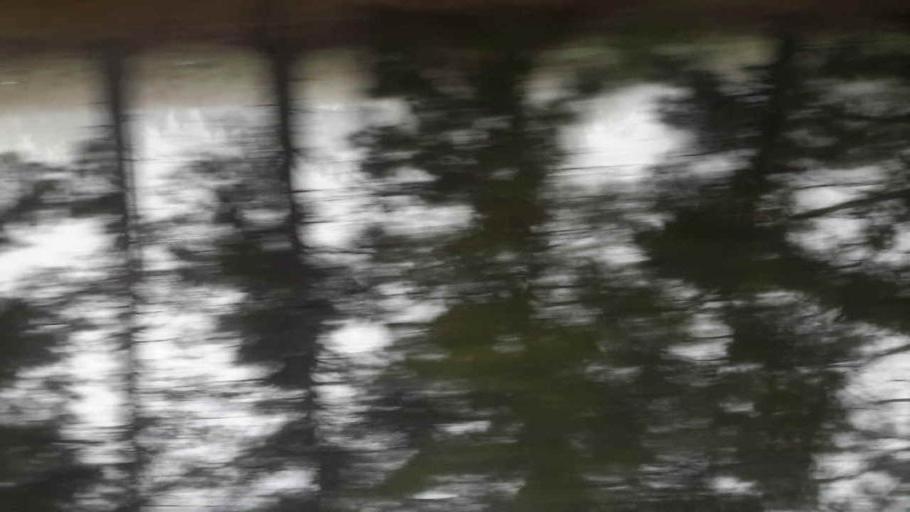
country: AU
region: New South Wales
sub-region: Wollondilly
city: Douglas Park
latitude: -34.2623
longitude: 150.7197
